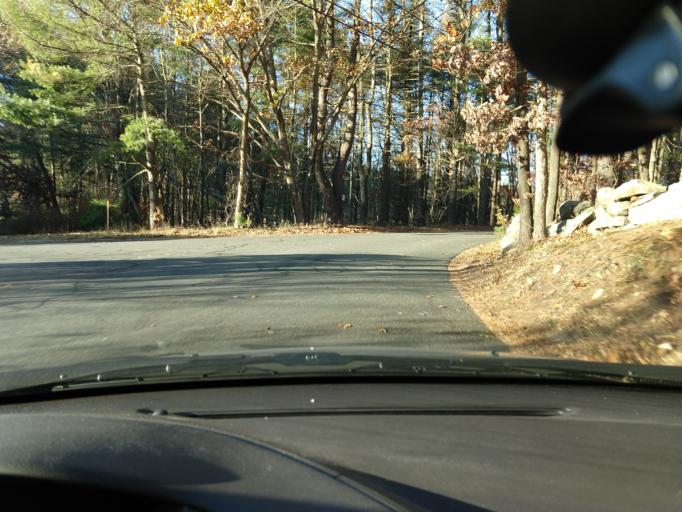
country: US
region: Massachusetts
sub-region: Middlesex County
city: Westford
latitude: 42.5409
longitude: -71.4185
